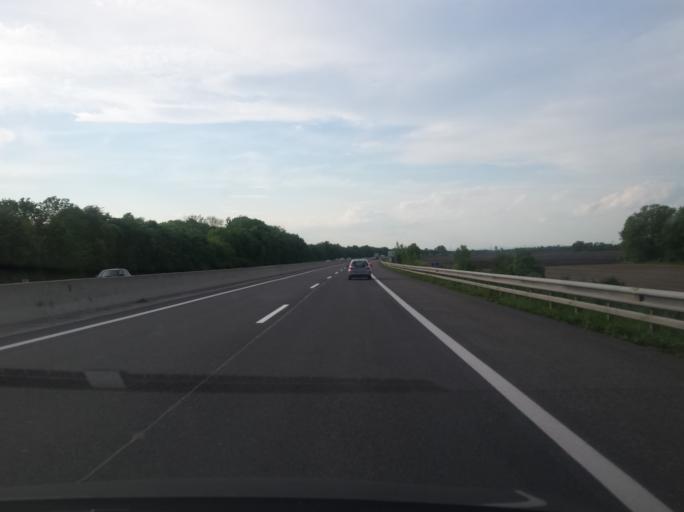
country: AT
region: Lower Austria
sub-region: Politischer Bezirk Baden
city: Ebreichsdorf
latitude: 47.9471
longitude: 16.3704
